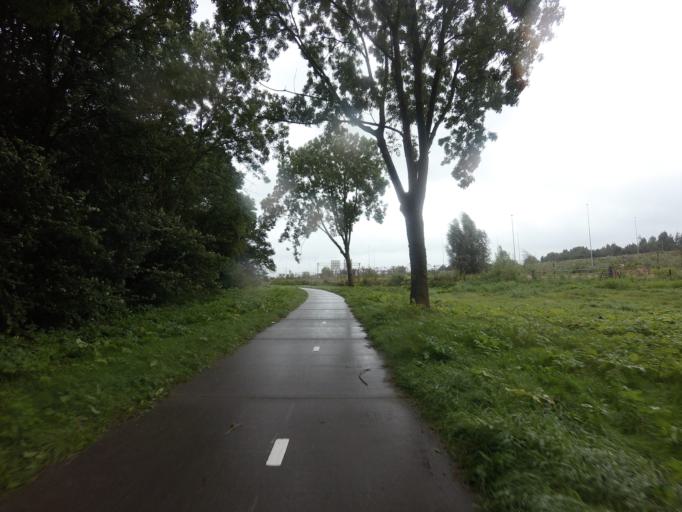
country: NL
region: North Holland
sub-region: Gemeente Naarden
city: Naarden
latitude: 52.3387
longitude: 5.1698
